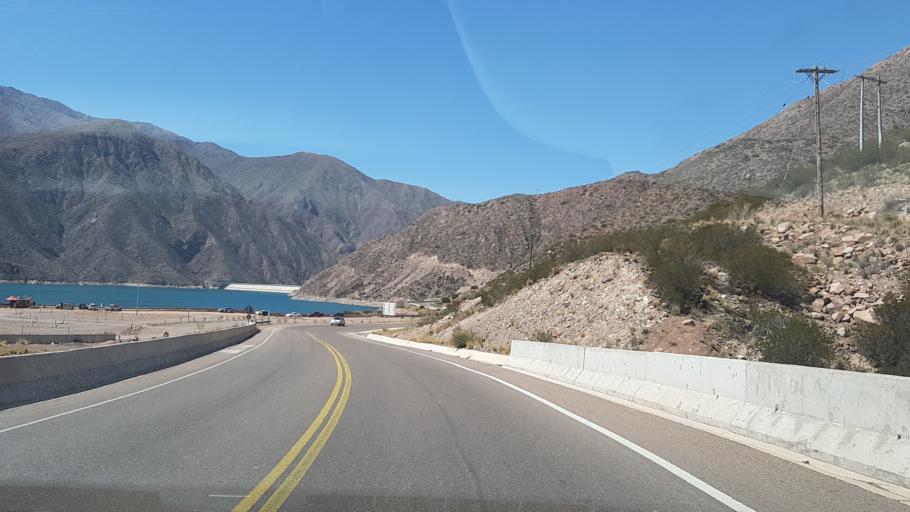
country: AR
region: Mendoza
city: Lujan de Cuyo
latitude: -32.9952
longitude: -69.1466
